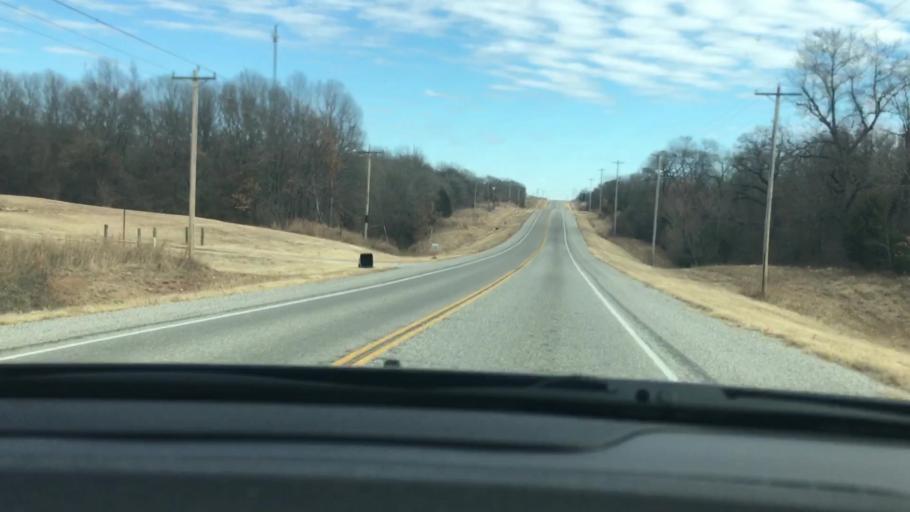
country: US
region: Oklahoma
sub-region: Garvin County
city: Stratford
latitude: 34.7967
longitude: -97.0113
